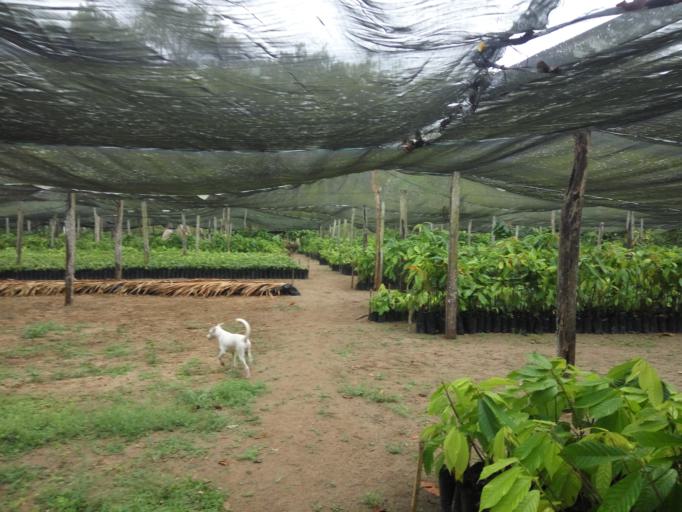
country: MX
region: Tabasco
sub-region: Comalcalco
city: Oriente 2da. Seccion (San Cayetano)
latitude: 18.1827
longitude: -93.2412
